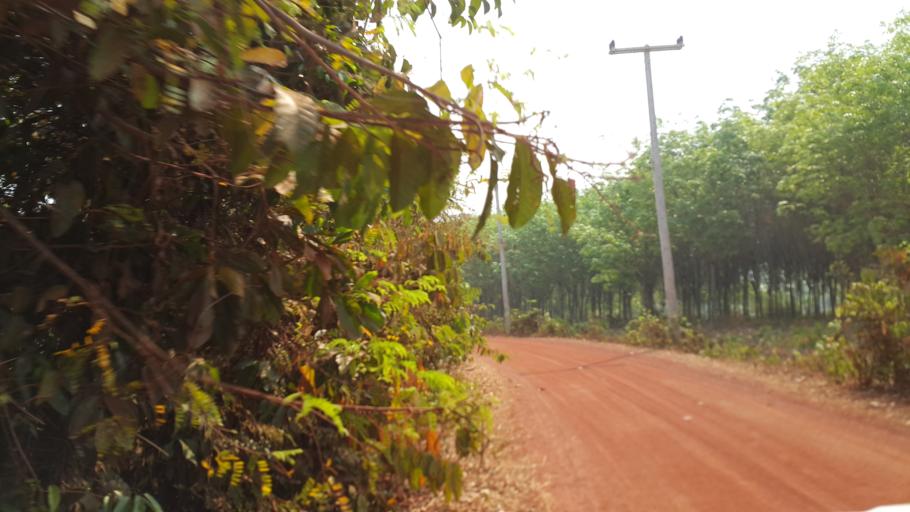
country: TH
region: Nakhon Phanom
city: Ban Phaeng
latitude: 17.8302
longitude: 104.2493
